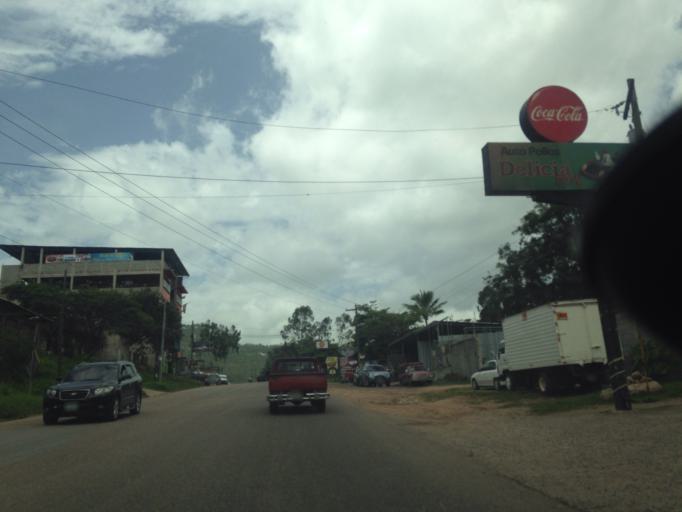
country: HN
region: Francisco Morazan
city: El Tablon
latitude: 14.0462
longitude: -87.1519
